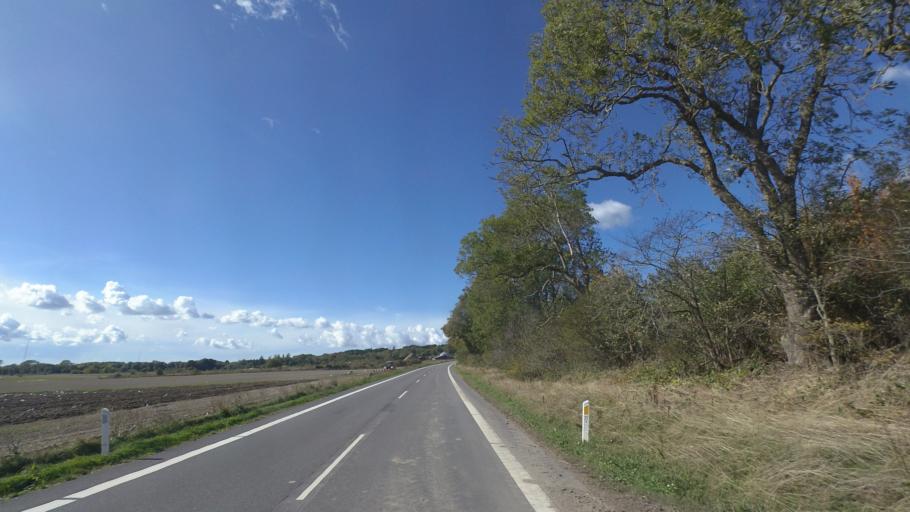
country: DK
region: Capital Region
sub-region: Bornholm Kommune
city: Nexo
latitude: 55.0626
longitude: 15.0298
